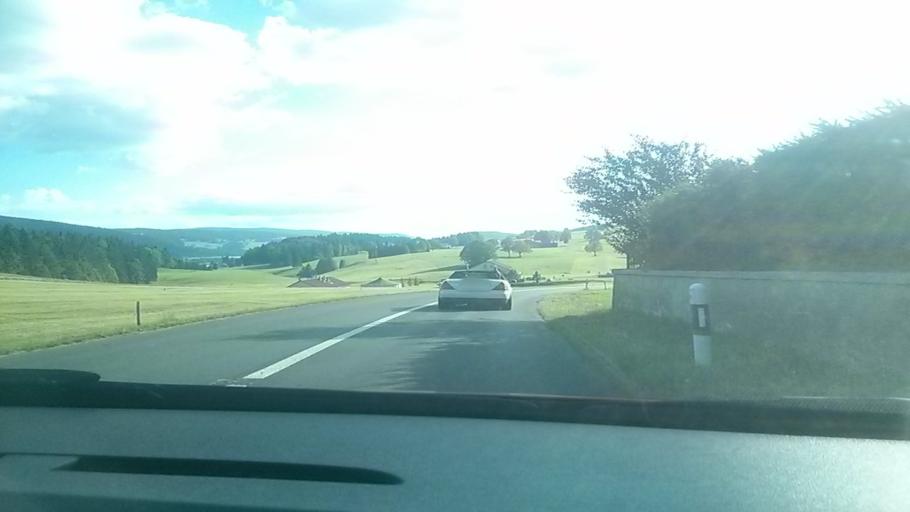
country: CH
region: Vaud
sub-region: Jura-Nord vaudois District
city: Le Chenit
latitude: 46.6215
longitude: 6.2404
